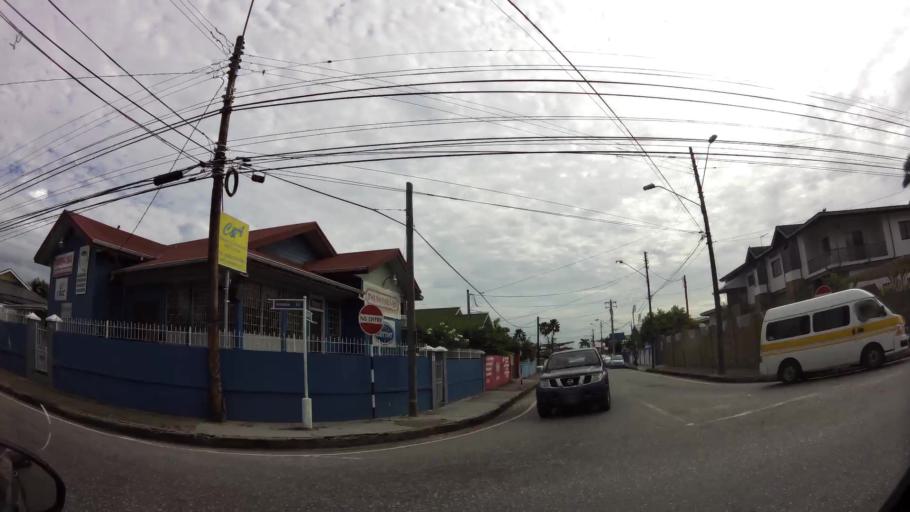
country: TT
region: City of Port of Spain
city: Mucurapo
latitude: 10.6662
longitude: -61.5297
